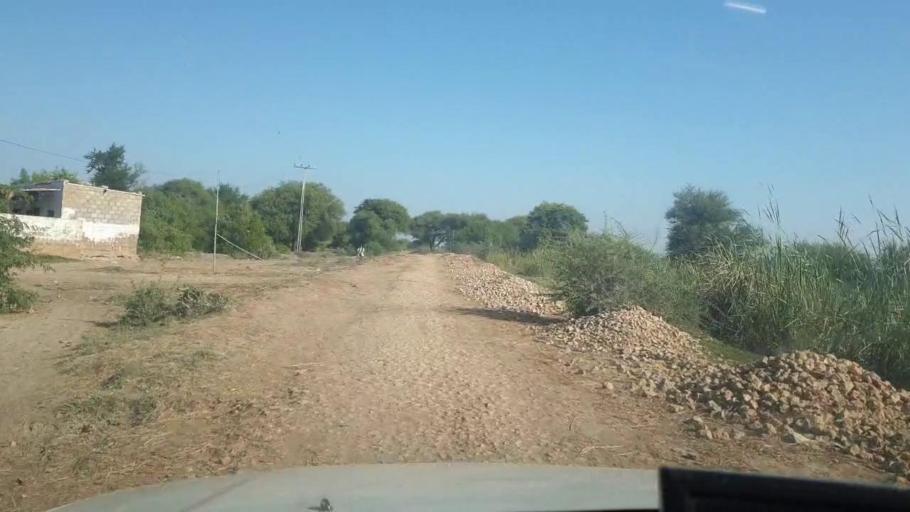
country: PK
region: Sindh
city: Mirpur Sakro
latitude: 24.4990
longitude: 67.6243
